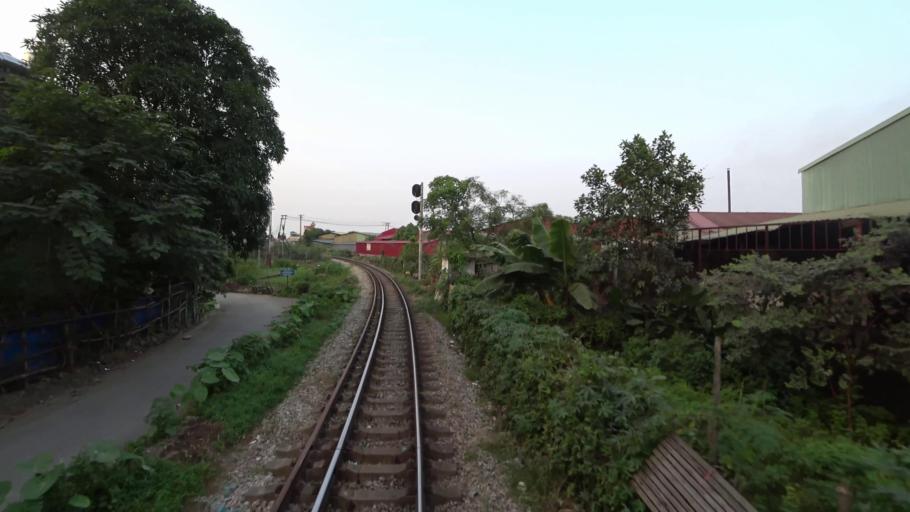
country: VN
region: Ha Noi
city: Dong Anh
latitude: 21.1082
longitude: 105.8985
